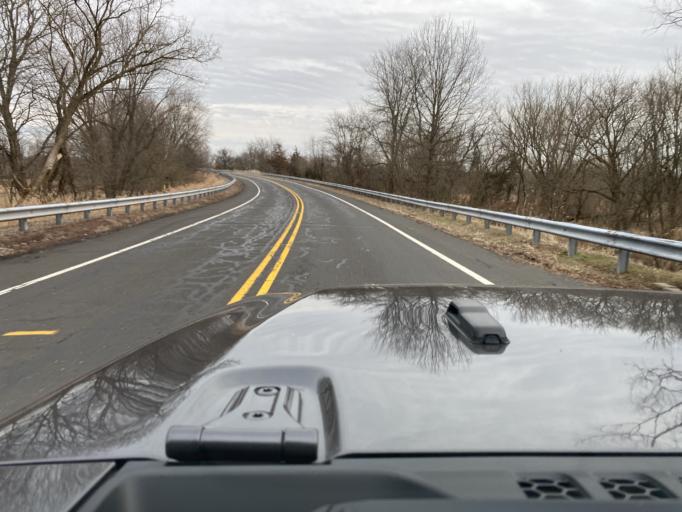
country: US
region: New Jersey
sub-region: Somerset County
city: Bloomingdale
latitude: 40.5167
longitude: -74.7325
